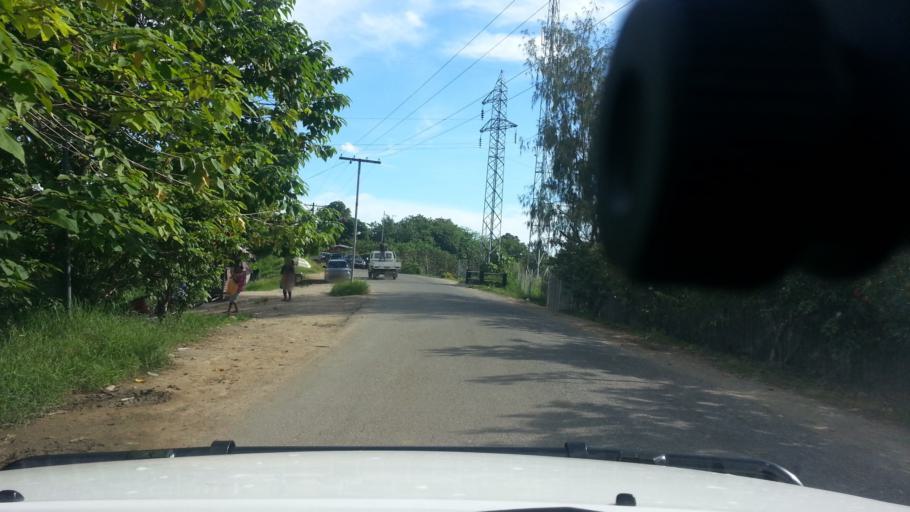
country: SB
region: Guadalcanal
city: Honiara
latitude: -9.4445
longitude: 159.9805
